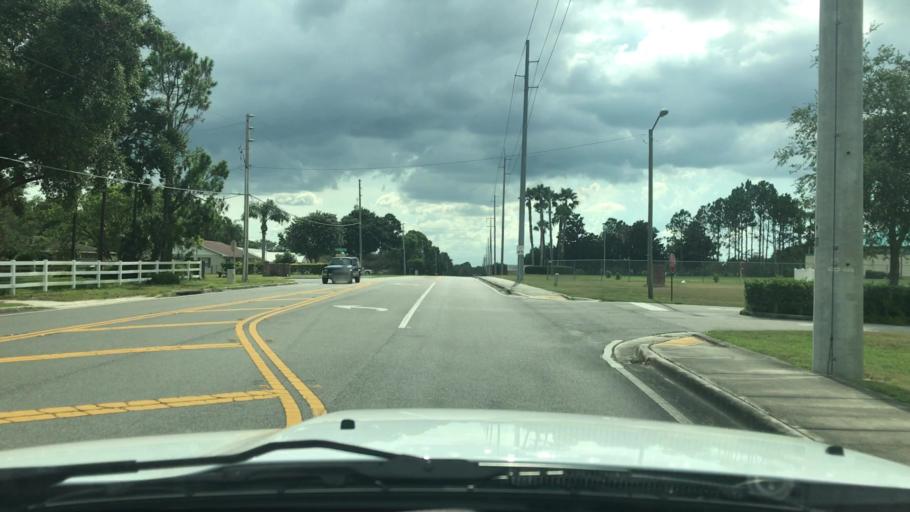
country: US
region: Florida
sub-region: Polk County
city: Cypress Gardens
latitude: 28.0151
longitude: -81.6623
